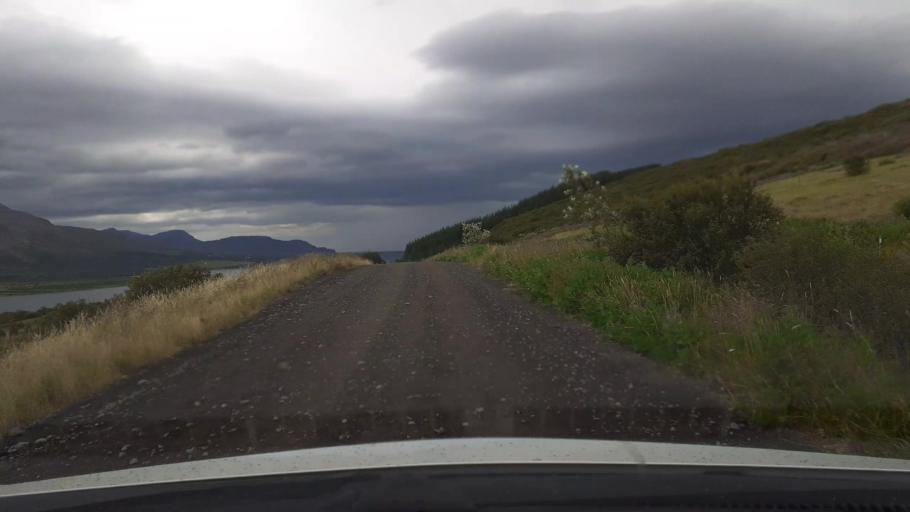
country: IS
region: Capital Region
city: Mosfellsbaer
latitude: 64.5271
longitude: -21.4886
